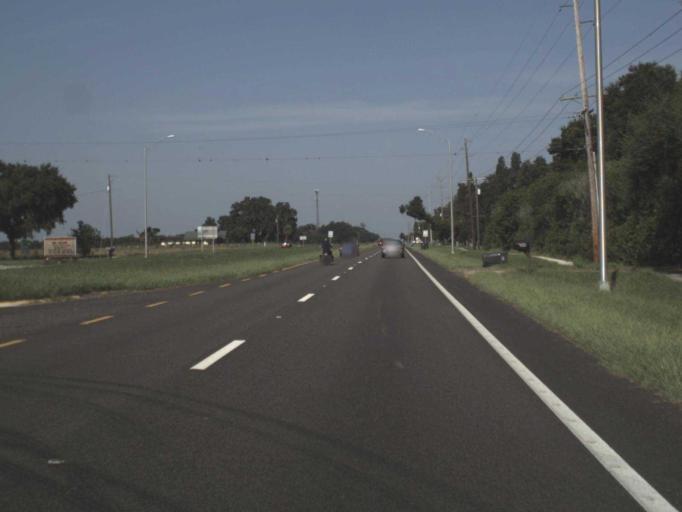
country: US
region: Florida
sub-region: Hillsborough County
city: Plant City
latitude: 27.9378
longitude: -82.1238
